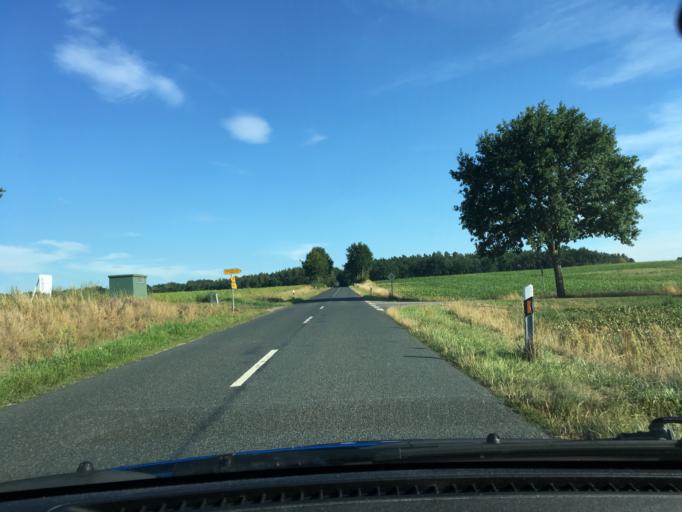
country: DE
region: Lower Saxony
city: Dahlenburg
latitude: 53.2121
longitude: 10.7039
